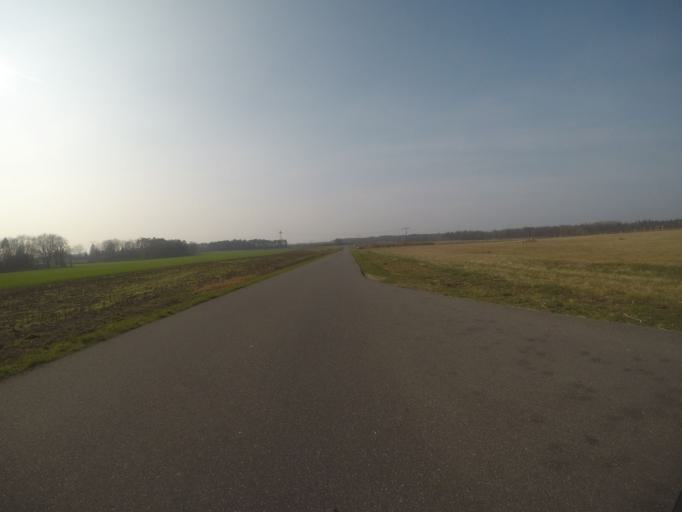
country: DE
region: Brandenburg
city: Rangsdorf
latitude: 52.3436
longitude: 13.4542
